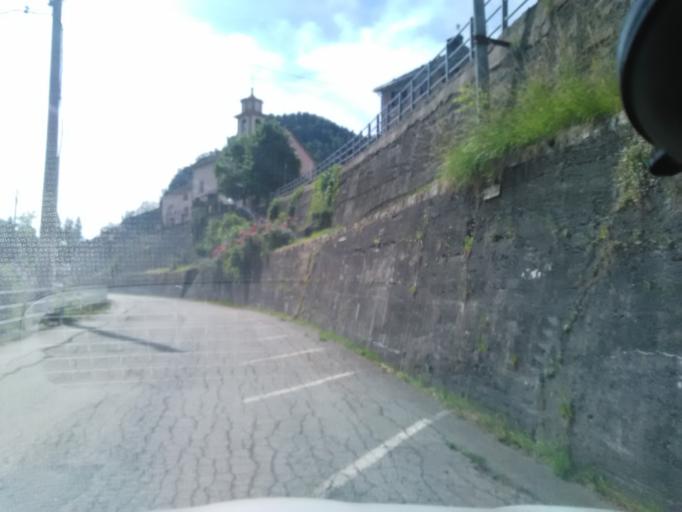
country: IT
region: Piedmont
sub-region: Provincia di Vercelli
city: Cervatto
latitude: 45.8835
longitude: 8.1617
